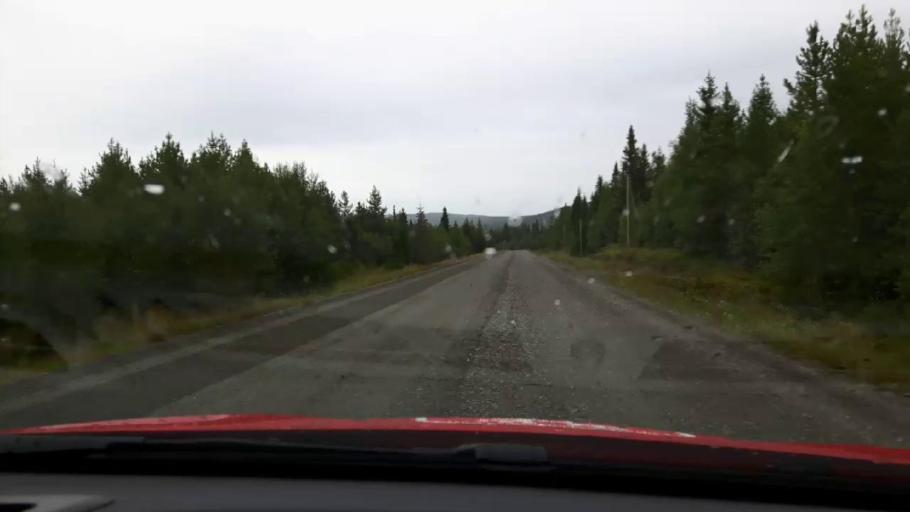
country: SE
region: Jaemtland
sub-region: Are Kommun
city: Are
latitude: 63.4087
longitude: 12.7973
